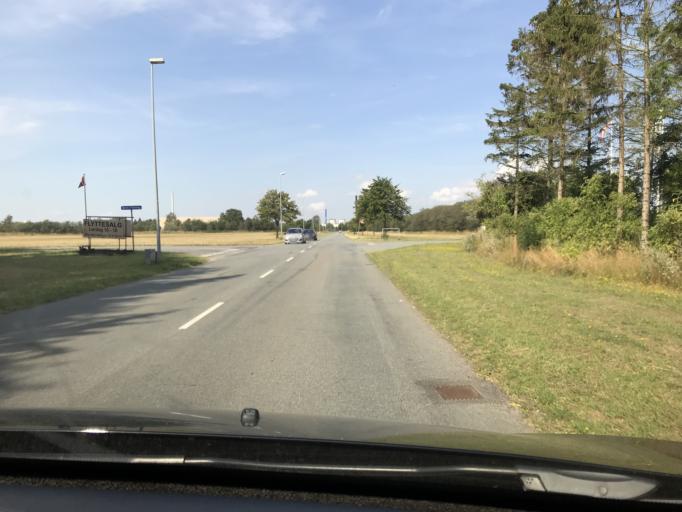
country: DK
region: Central Jutland
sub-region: Norddjurs Kommune
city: Auning
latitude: 56.4240
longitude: 10.3881
